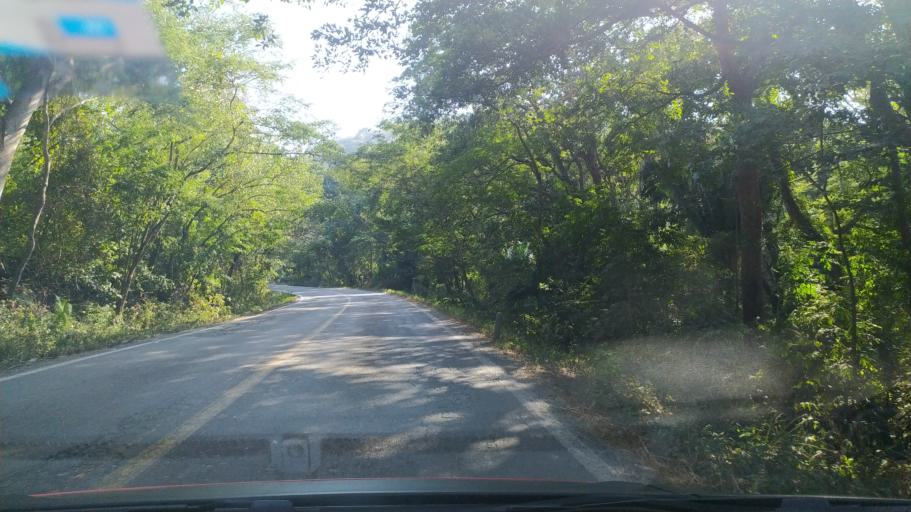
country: MX
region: Michoacan
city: Coahuayana Viejo
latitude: 18.6216
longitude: -103.6780
